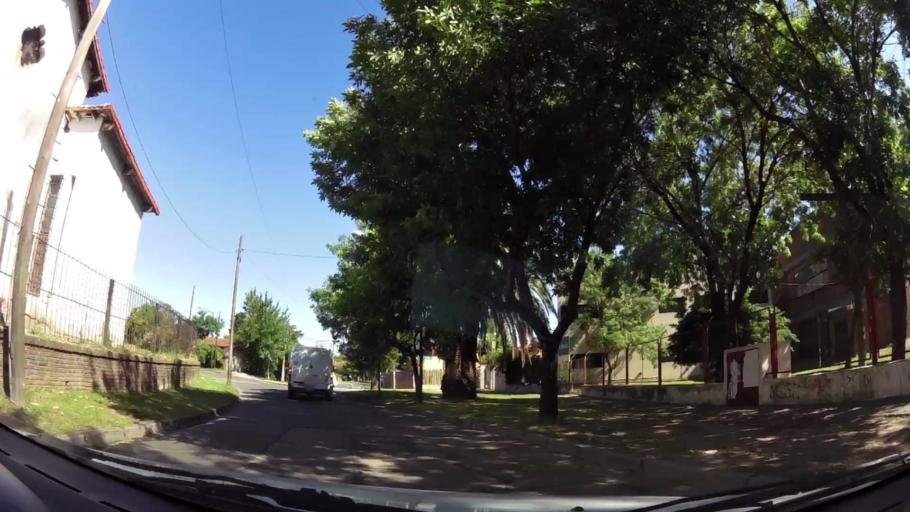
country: AR
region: Buenos Aires
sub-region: Partido de San Isidro
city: San Isidro
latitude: -34.4712
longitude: -58.5311
